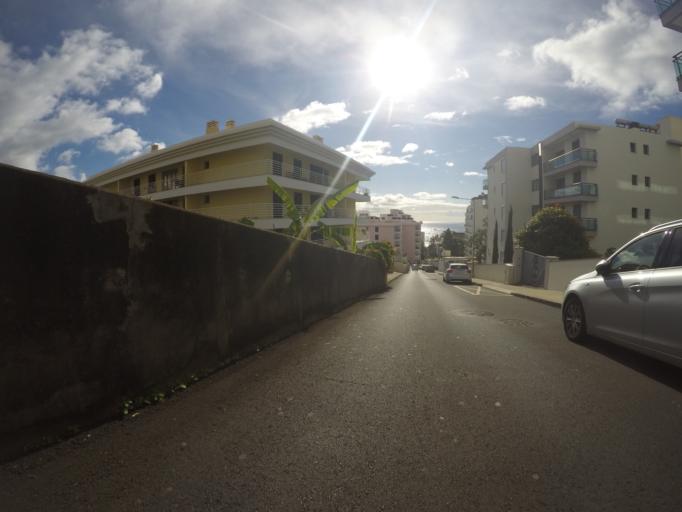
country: PT
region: Madeira
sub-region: Funchal
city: Funchal
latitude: 32.6406
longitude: -16.9298
